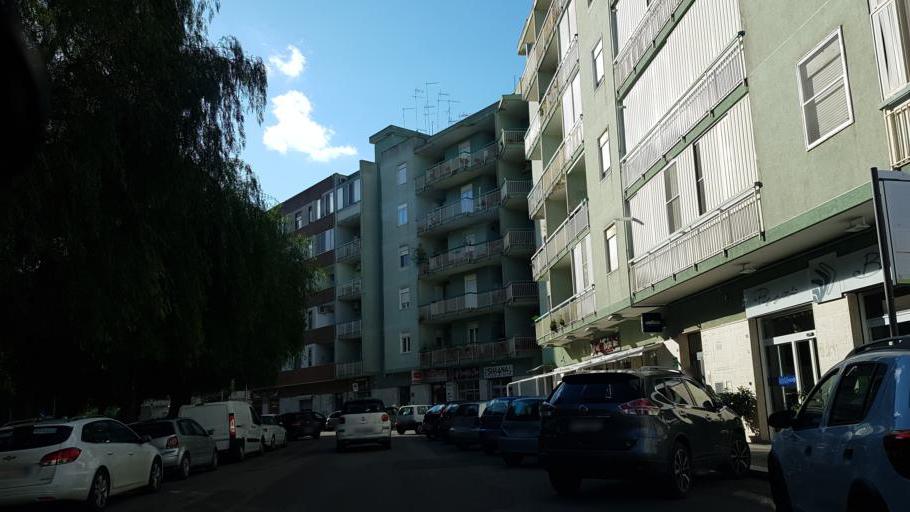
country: IT
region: Apulia
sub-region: Provincia di Brindisi
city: Brindisi
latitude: 40.6254
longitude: 17.9243
